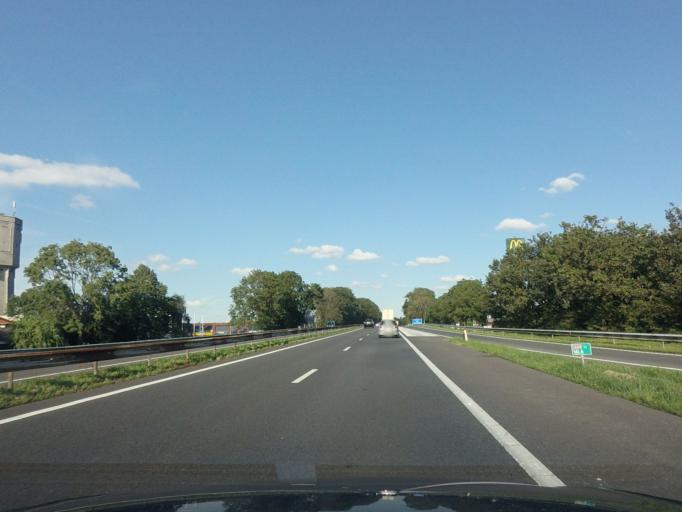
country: NL
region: South Holland
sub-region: Gemeente Teylingen
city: Sassenheim
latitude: 52.2146
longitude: 4.5124
